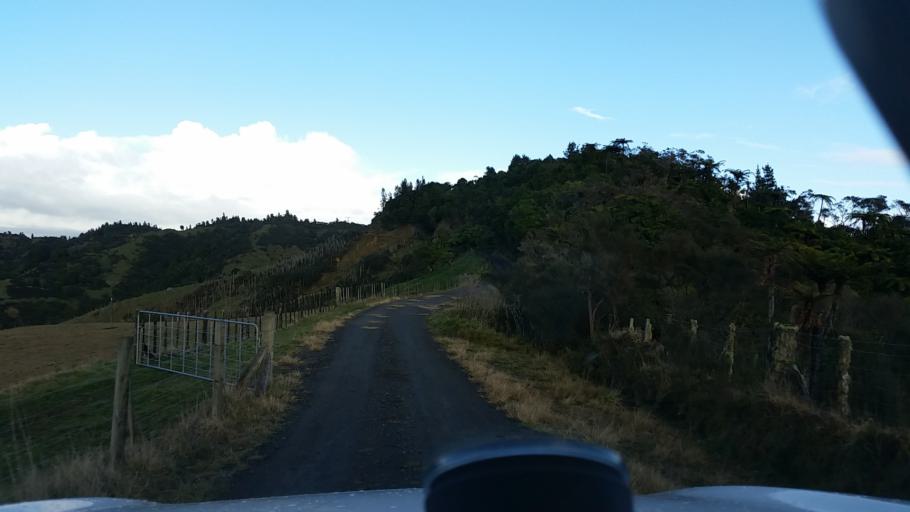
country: NZ
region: Taranaki
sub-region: South Taranaki District
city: Eltham
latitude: -39.4142
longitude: 174.5632
